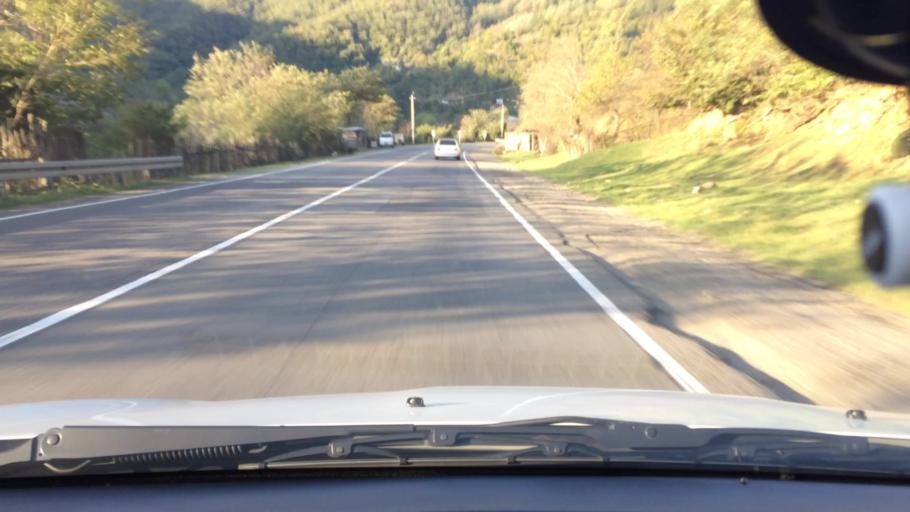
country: GE
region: Imereti
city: Kharagauli
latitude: 42.1056
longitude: 43.3166
